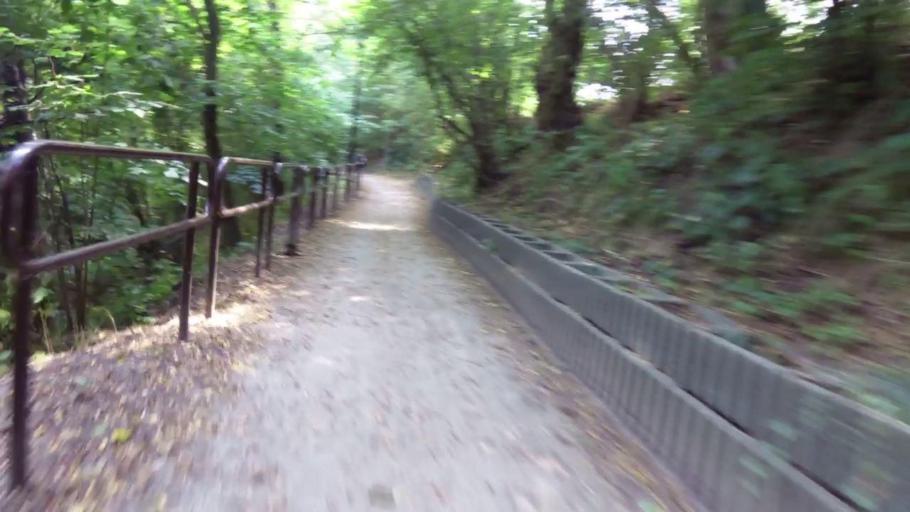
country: PL
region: West Pomeranian Voivodeship
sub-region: Powiat choszczenski
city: Choszczno
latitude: 53.1562
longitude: 15.4272
